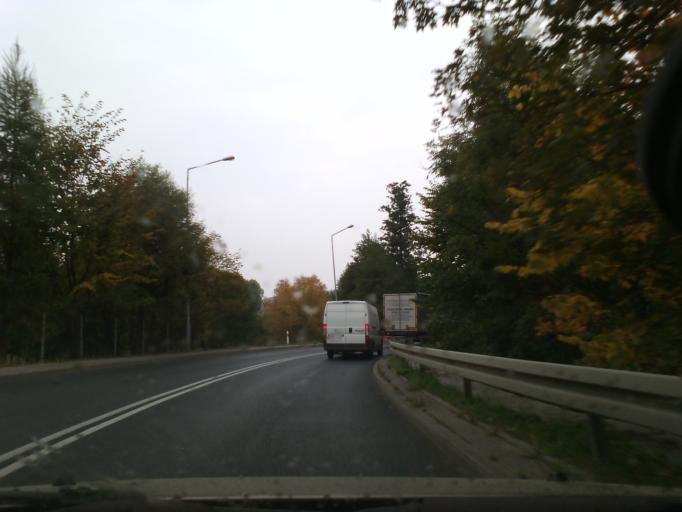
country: PL
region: Lower Silesian Voivodeship
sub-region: Powiat jeleniogorski
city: Janowice Wielkie
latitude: 50.9112
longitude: 15.9597
